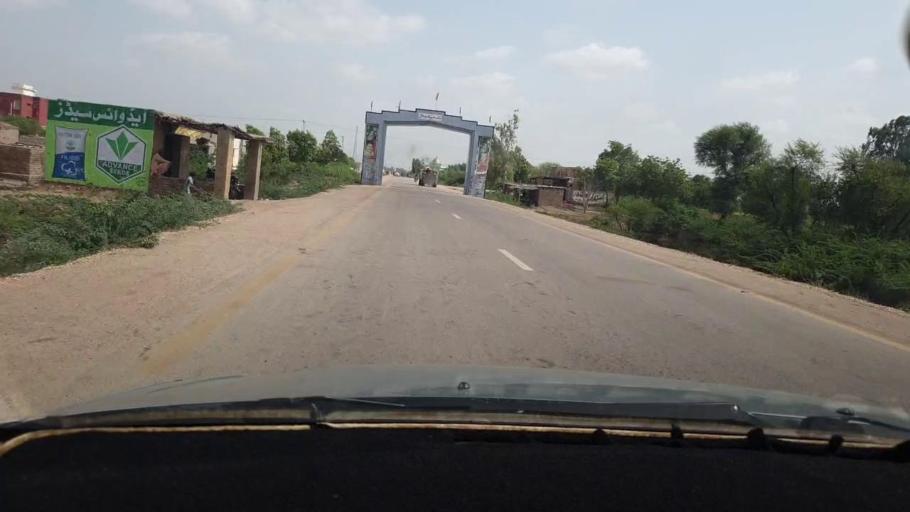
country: PK
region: Sindh
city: Digri
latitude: 25.0838
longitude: 69.2022
